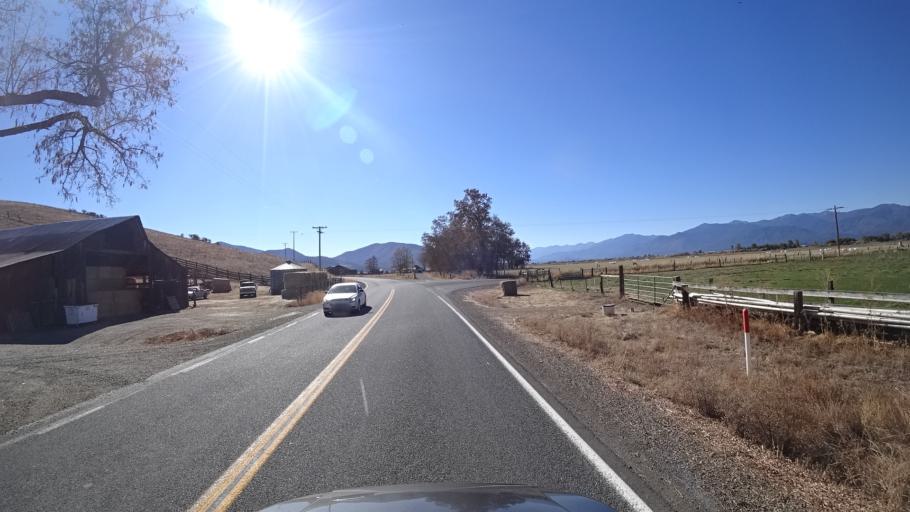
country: US
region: California
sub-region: Siskiyou County
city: Yreka
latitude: 41.5710
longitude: -122.8361
